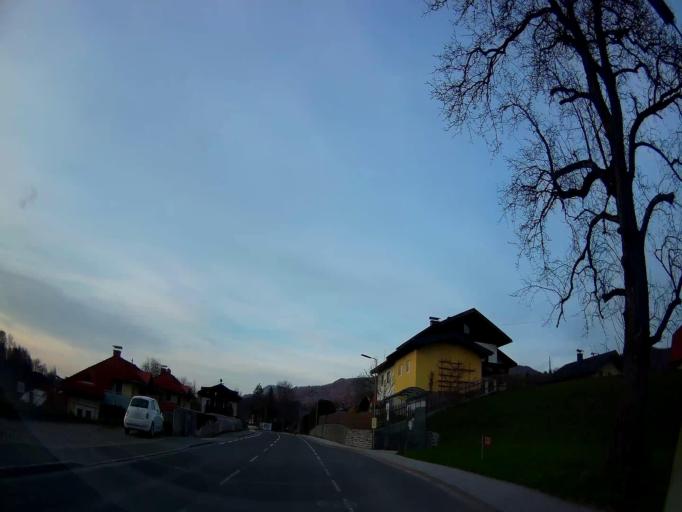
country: AT
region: Salzburg
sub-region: Politischer Bezirk Hallein
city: Puch bei Hallein
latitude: 47.7180
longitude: 13.0912
